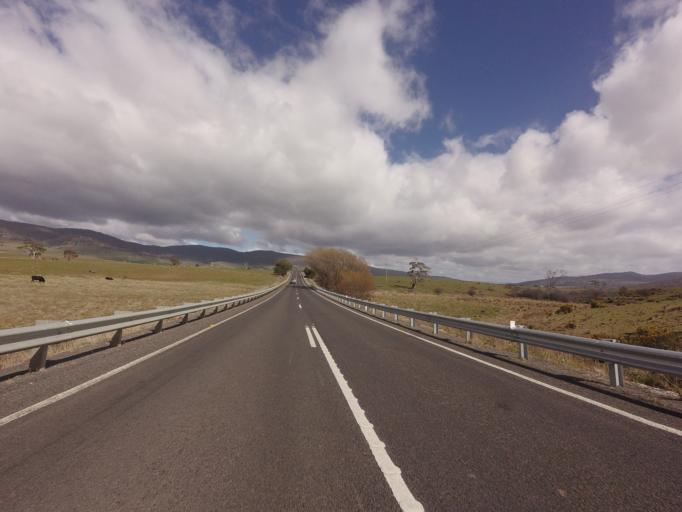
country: AU
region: Tasmania
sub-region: Northern Midlands
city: Evandale
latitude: -41.8041
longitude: 147.6834
